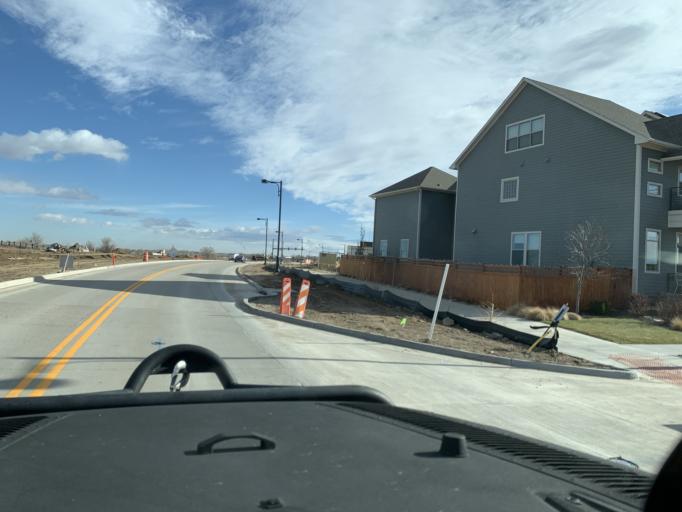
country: US
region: Colorado
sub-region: Adams County
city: Aurora
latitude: 39.7577
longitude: -104.8565
